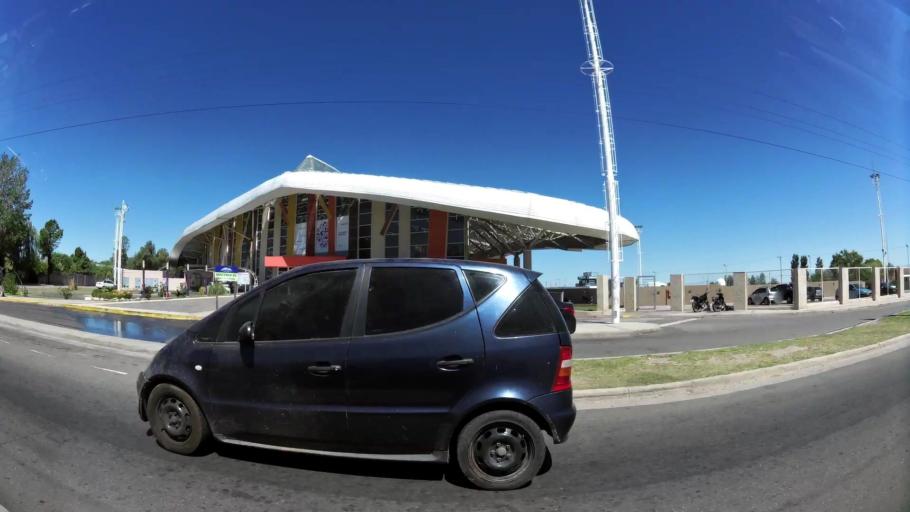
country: AR
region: San Luis
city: San Luis
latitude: -33.2941
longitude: -66.2972
